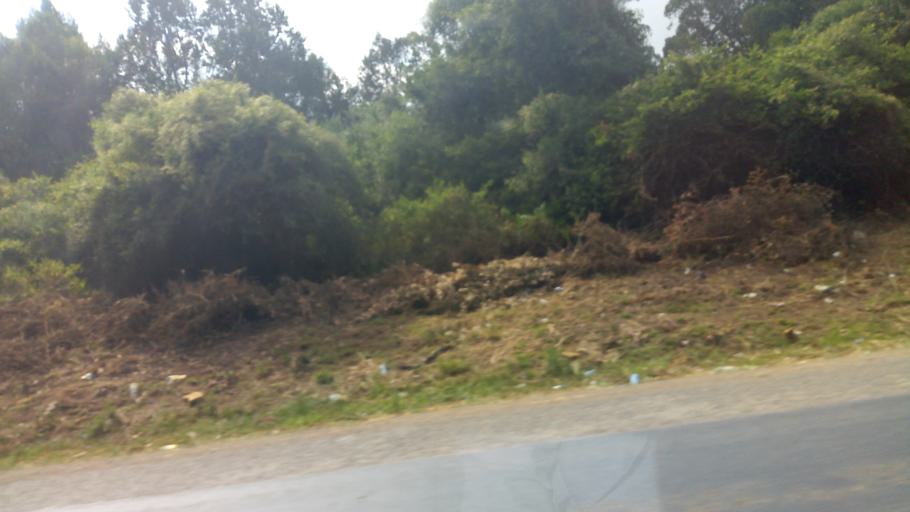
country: KE
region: Kiambu
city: Limuru
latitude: -1.0764
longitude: 36.6022
